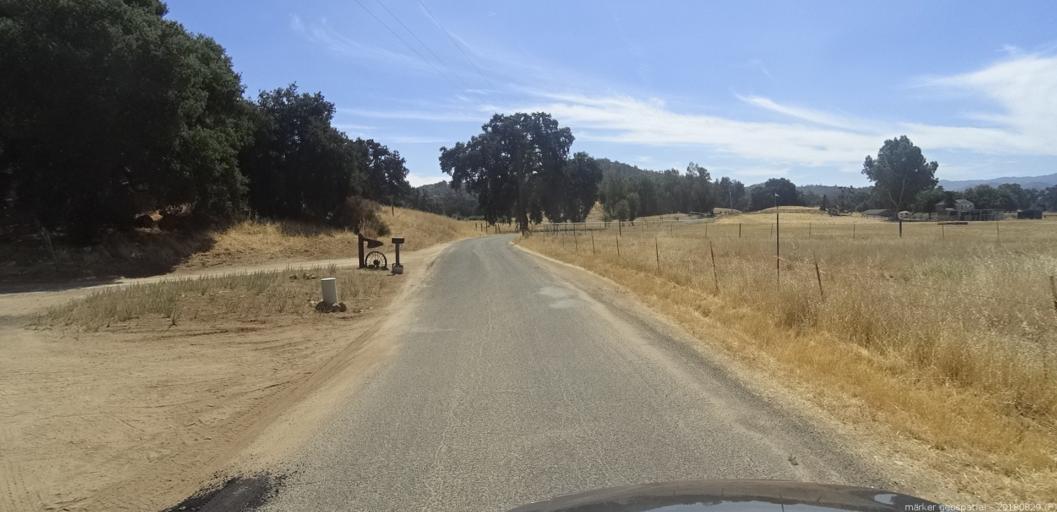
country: US
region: California
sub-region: San Luis Obispo County
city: Lake Nacimiento
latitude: 35.8135
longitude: -121.0908
